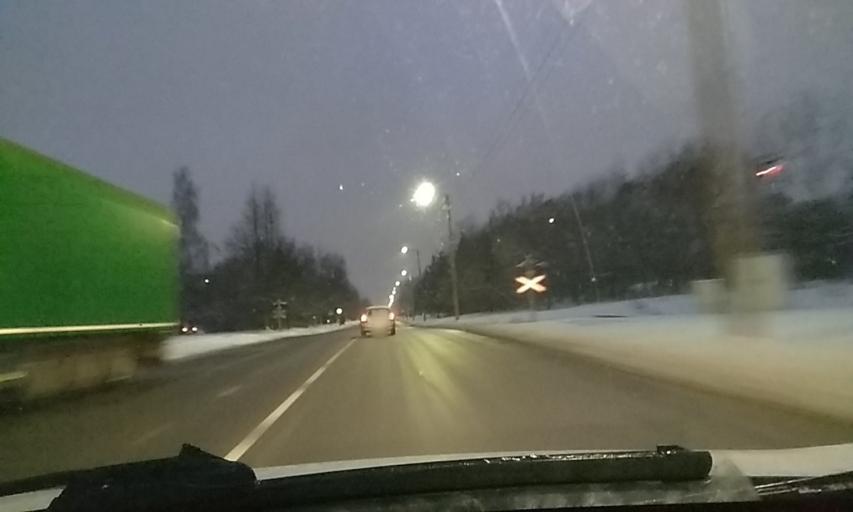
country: LT
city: Ramuciai
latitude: 54.9130
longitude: 24.0143
